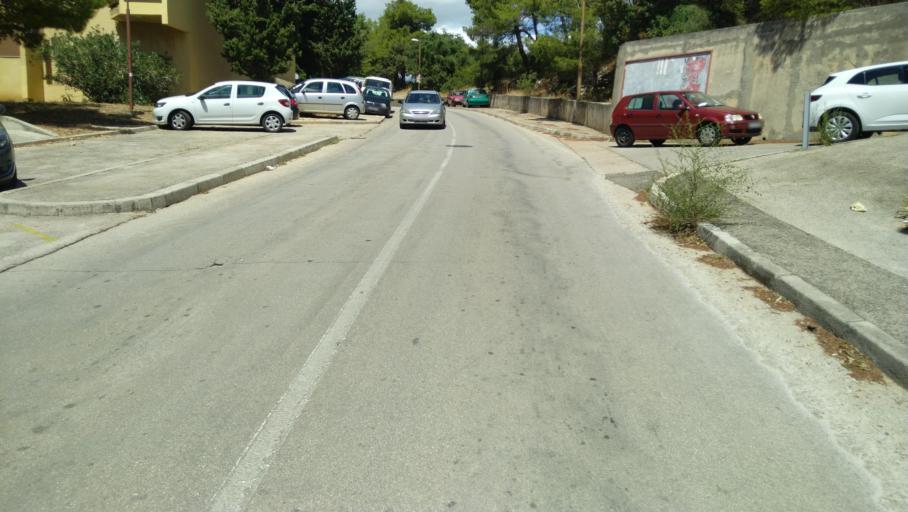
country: HR
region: Sibensko-Kniniska
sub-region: Grad Sibenik
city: Sibenik
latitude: 43.7202
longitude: 15.9122
